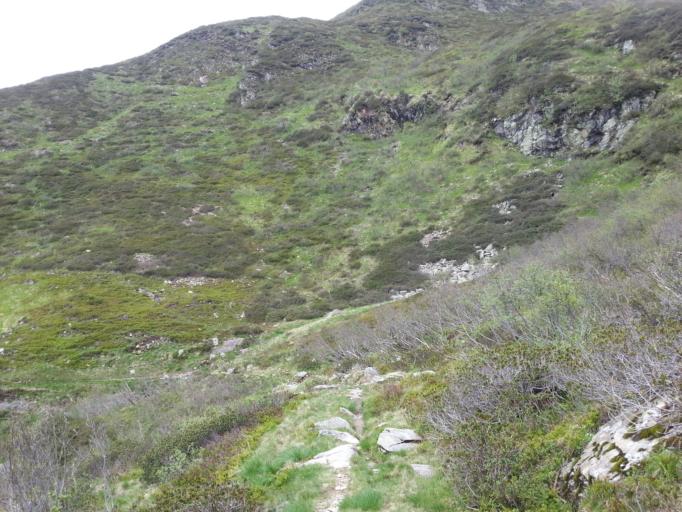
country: IT
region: Lombardy
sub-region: Provincia di Varese
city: Curiglia
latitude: 46.0862
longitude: 8.8605
